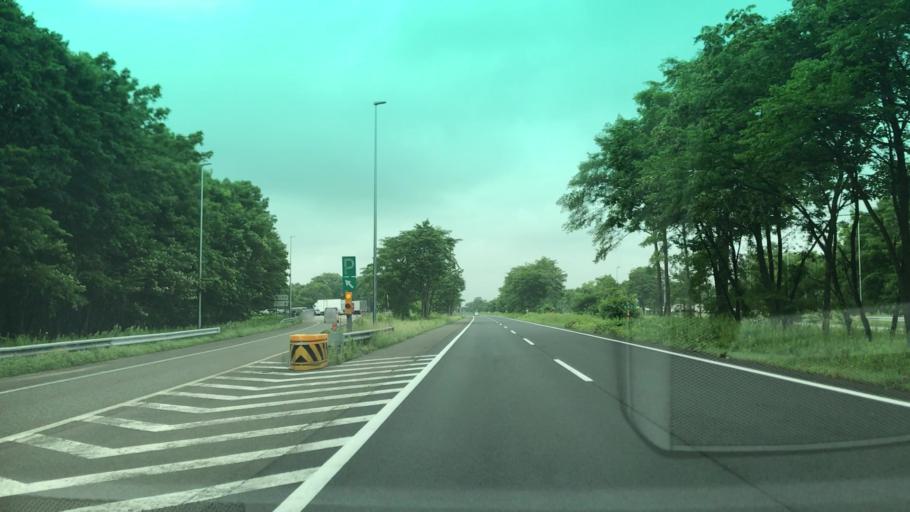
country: JP
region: Hokkaido
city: Chitose
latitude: 42.7549
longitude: 141.6430
